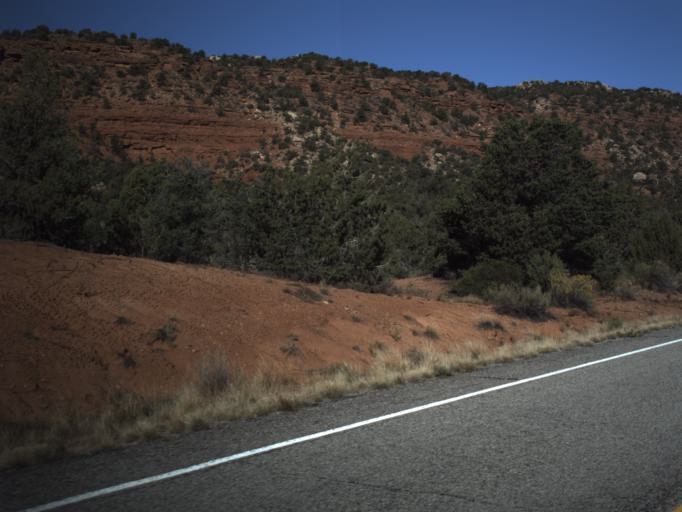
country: US
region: Utah
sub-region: San Juan County
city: Blanding
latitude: 37.5707
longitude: -110.0366
